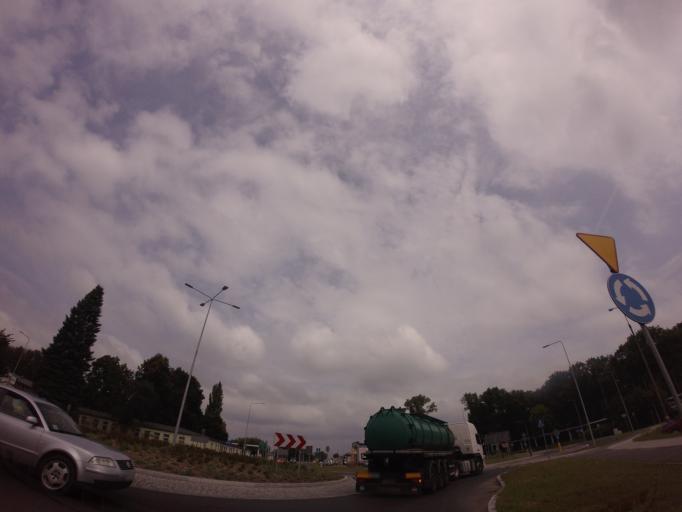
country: PL
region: Lesser Poland Voivodeship
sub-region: Powiat oswiecimski
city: Zaborze
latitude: 50.0385
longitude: 19.2536
